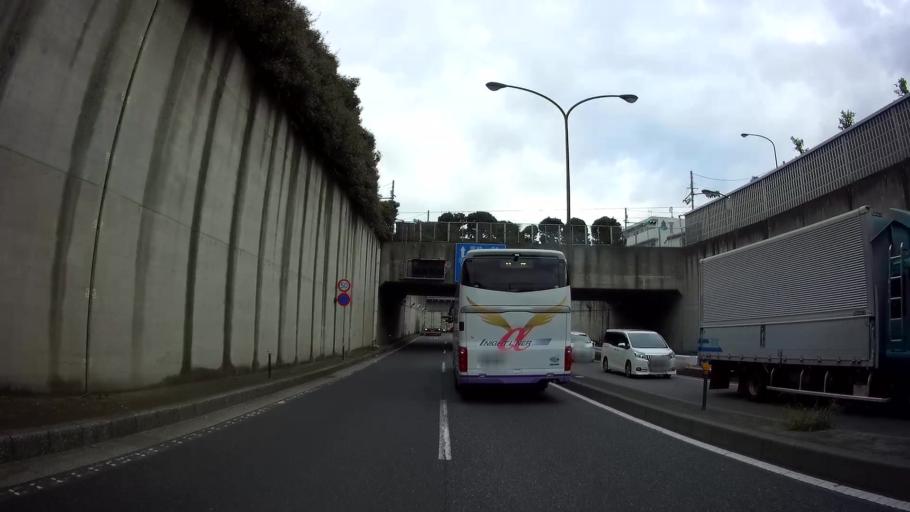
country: JP
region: Saitama
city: Wako
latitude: 35.7683
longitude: 139.6525
